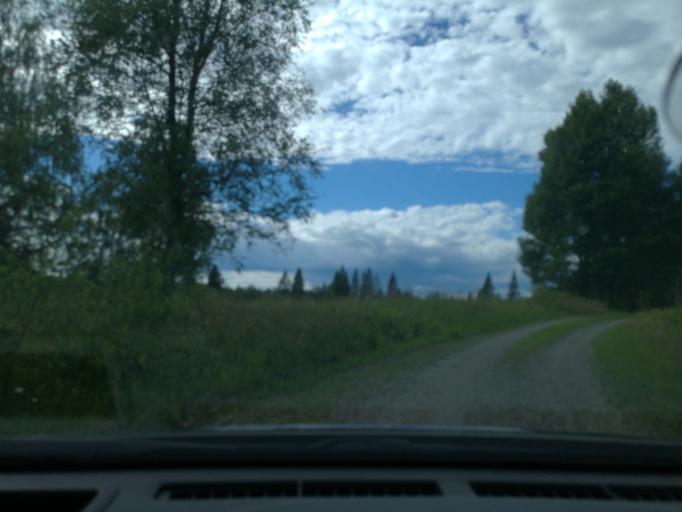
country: SE
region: Vaestmanland
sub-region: Surahammars Kommun
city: Ramnas
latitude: 59.8003
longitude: 16.3046
